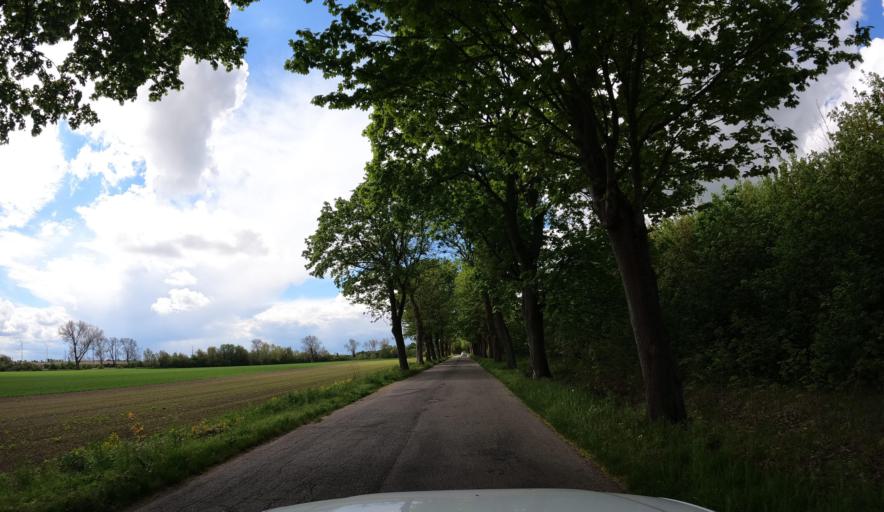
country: PL
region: West Pomeranian Voivodeship
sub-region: Powiat kamienski
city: Wolin
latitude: 53.8567
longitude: 14.6361
